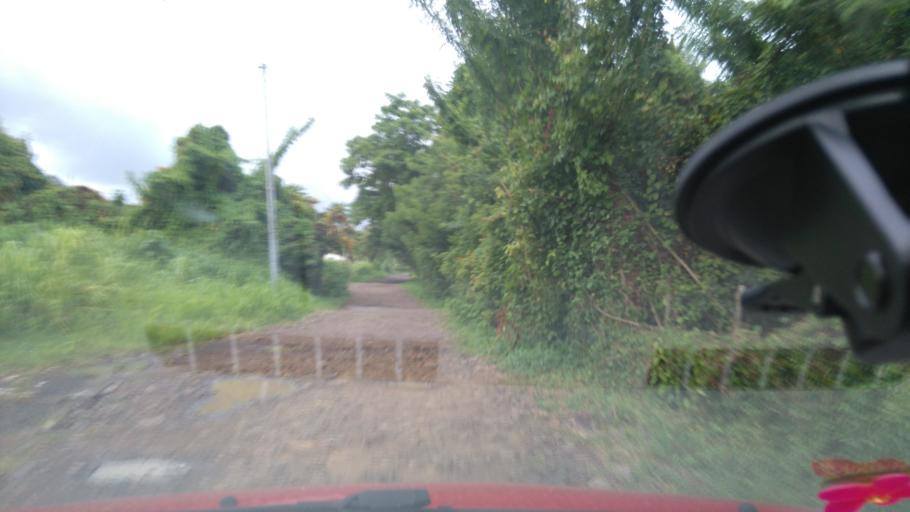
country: MQ
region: Martinique
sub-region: Martinique
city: Ducos
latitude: 14.5527
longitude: -60.9672
